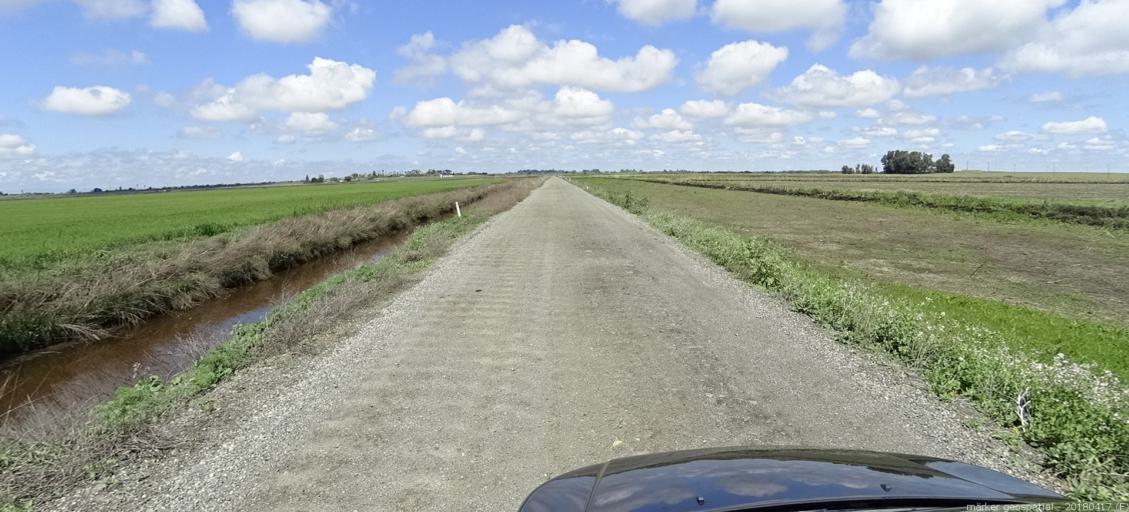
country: US
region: California
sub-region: Solano County
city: Rio Vista
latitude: 38.1349
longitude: -121.5805
